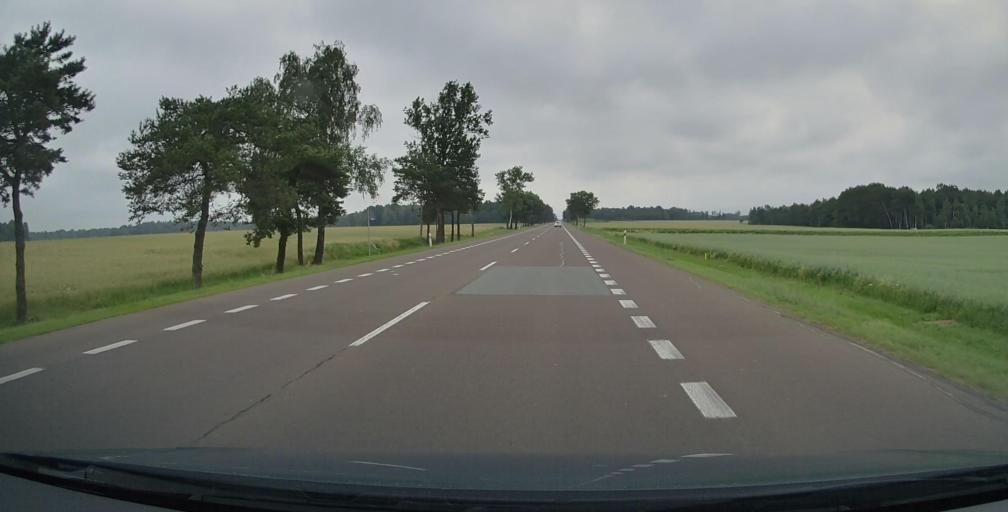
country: PL
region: Lublin Voivodeship
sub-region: Powiat bialski
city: Miedzyrzec Podlaski
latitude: 52.0069
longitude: 22.8282
